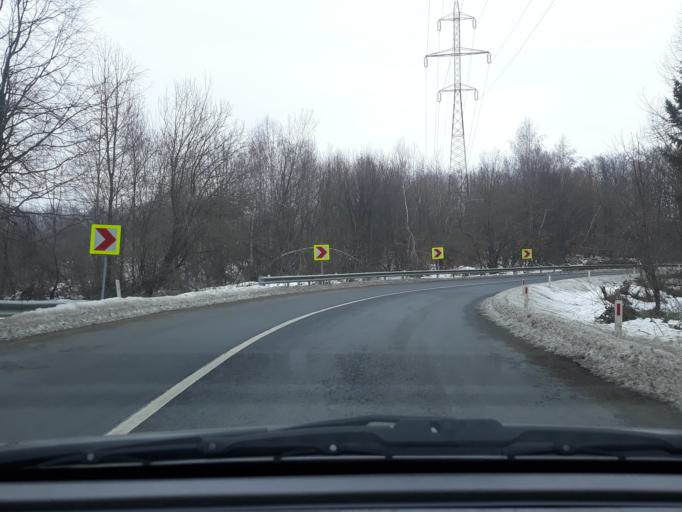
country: RO
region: Bihor
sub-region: Comuna Sinteu
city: Sinteu
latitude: 47.1214
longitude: 22.4471
